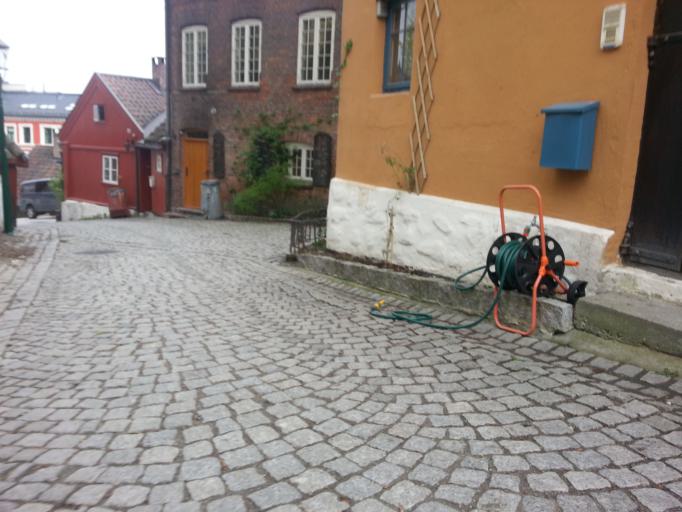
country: NO
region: Oslo
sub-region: Oslo
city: Oslo
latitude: 59.9201
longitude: 10.7475
